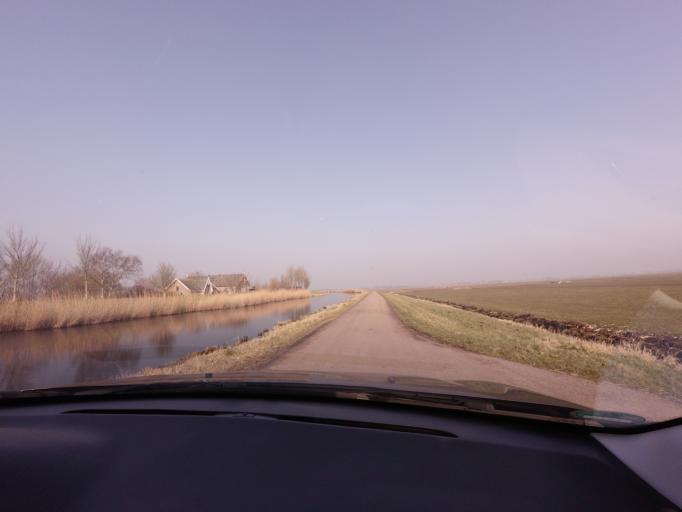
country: NL
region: North Holland
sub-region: Gemeente Beemster
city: Halfweg
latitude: 52.5827
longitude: 4.9544
